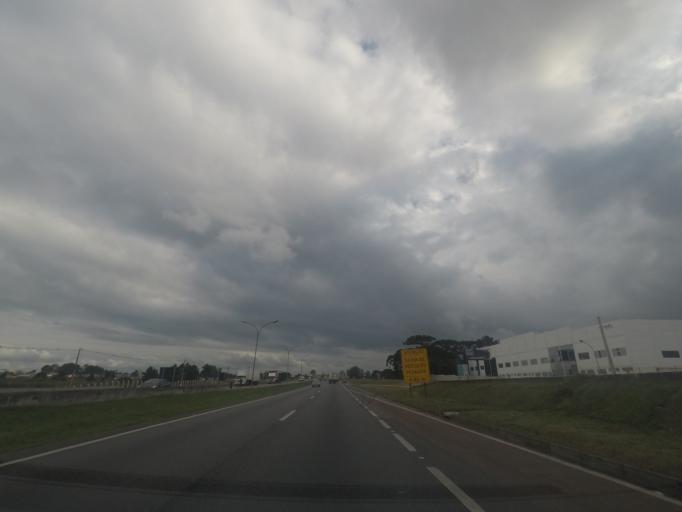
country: BR
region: Parana
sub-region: Sao Jose Dos Pinhais
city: Sao Jose dos Pinhais
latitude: -25.5275
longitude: -49.1410
